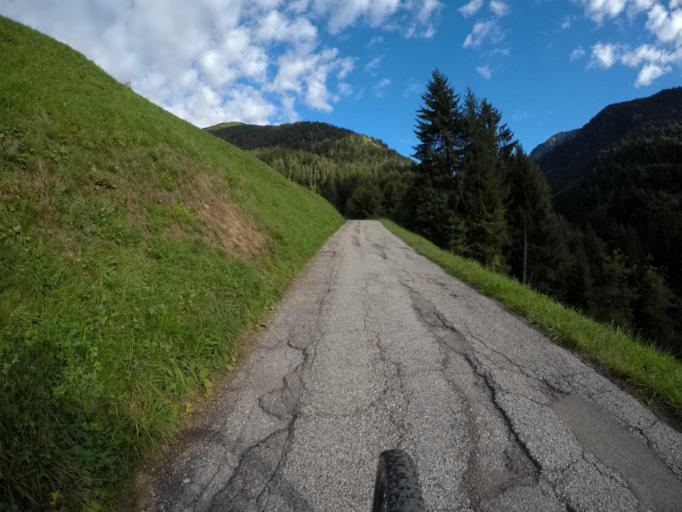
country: IT
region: Friuli Venezia Giulia
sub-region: Provincia di Udine
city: Paularo
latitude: 46.5410
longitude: 13.1181
